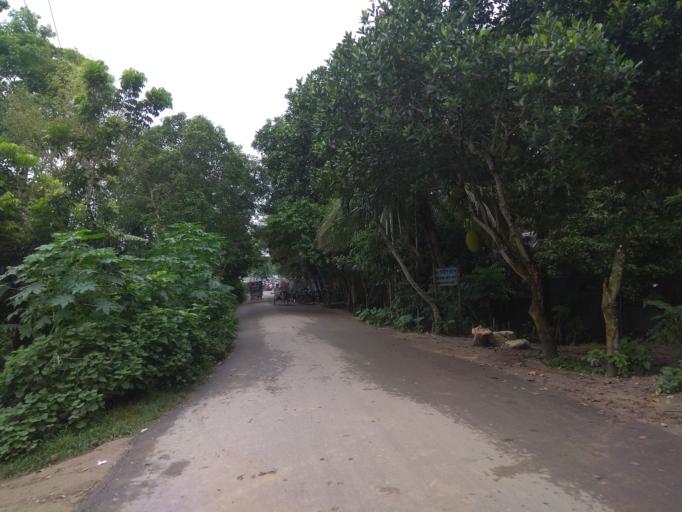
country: BD
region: Dhaka
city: Dohar
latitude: 23.4402
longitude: 90.0724
